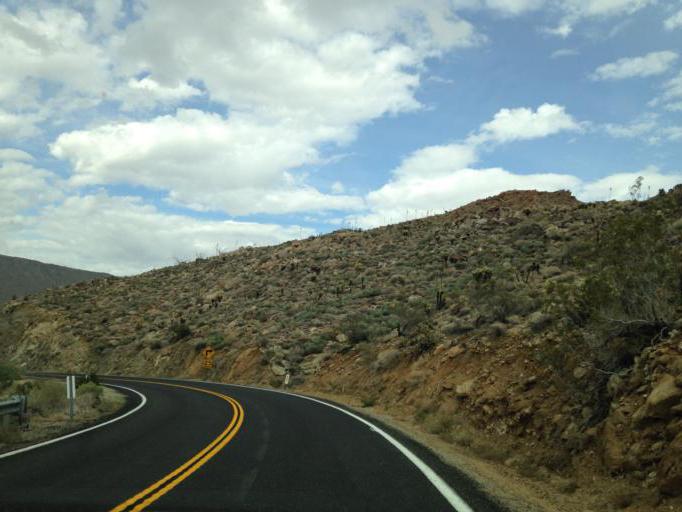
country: US
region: California
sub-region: San Diego County
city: Borrego Springs
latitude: 33.1268
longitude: -116.4349
